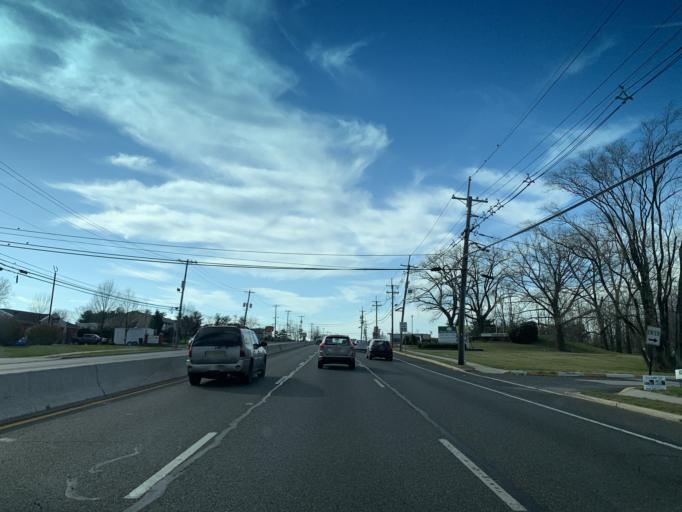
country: US
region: New Jersey
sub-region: Burlington County
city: Cinnaminson
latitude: 40.0104
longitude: -74.9657
